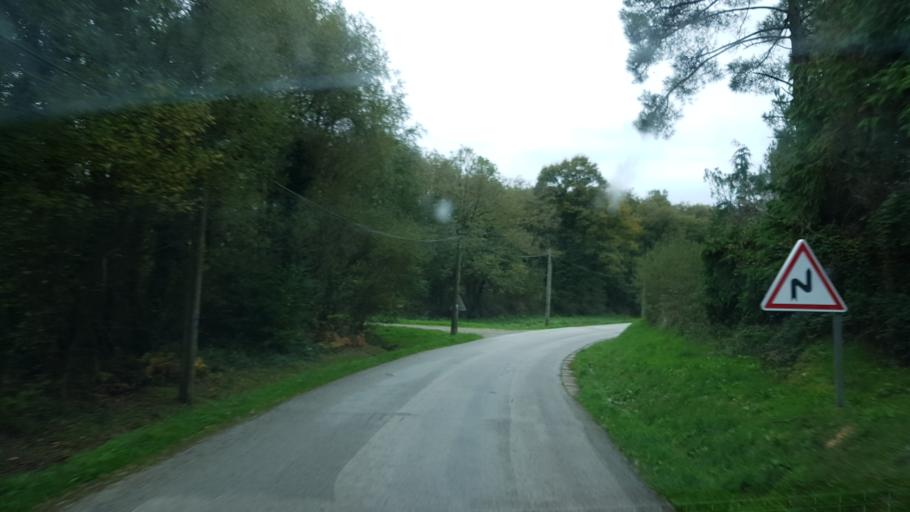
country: FR
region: Brittany
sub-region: Departement du Morbihan
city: Serent
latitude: 47.7805
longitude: -2.4957
